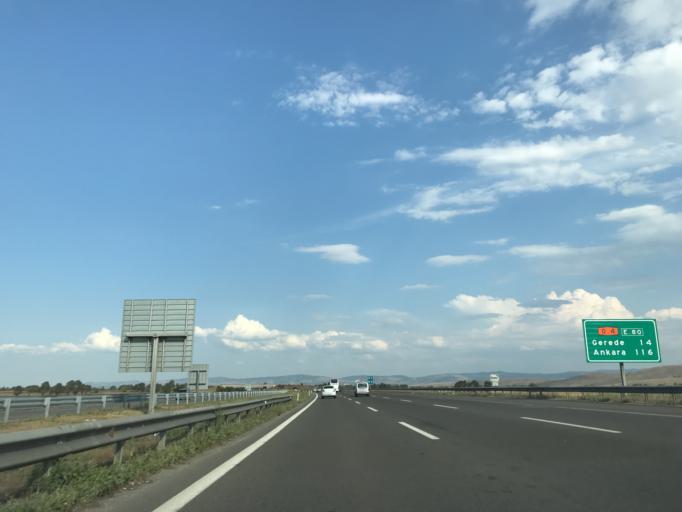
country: TR
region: Bolu
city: Dortdivan
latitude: 40.7404
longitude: 32.1314
